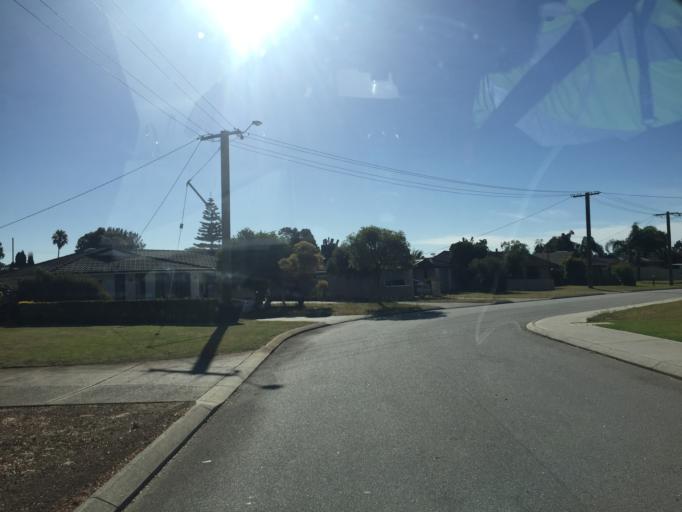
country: AU
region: Western Australia
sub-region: Canning
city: East Cannington
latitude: -32.0150
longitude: 115.9671
